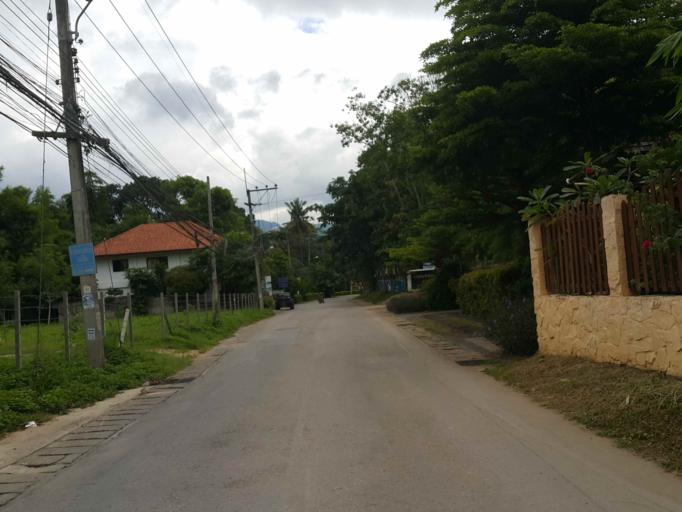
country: TH
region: Chiang Mai
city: San Sai
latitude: 18.9122
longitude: 98.9333
